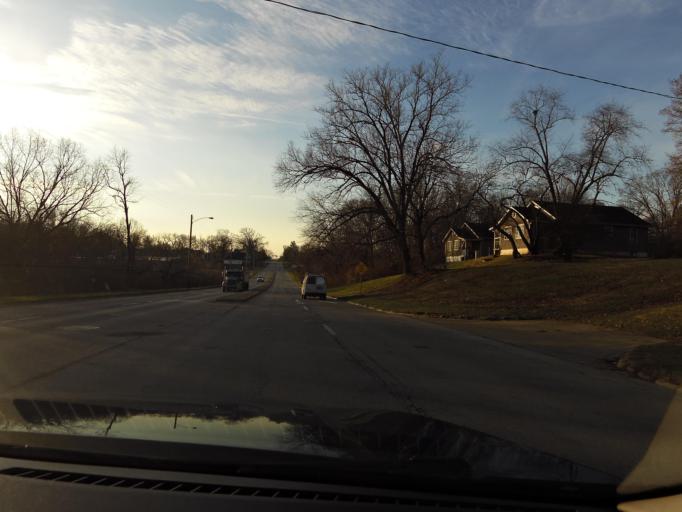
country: US
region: Illinois
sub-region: Fayette County
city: Vandalia
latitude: 38.9689
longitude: -89.0932
